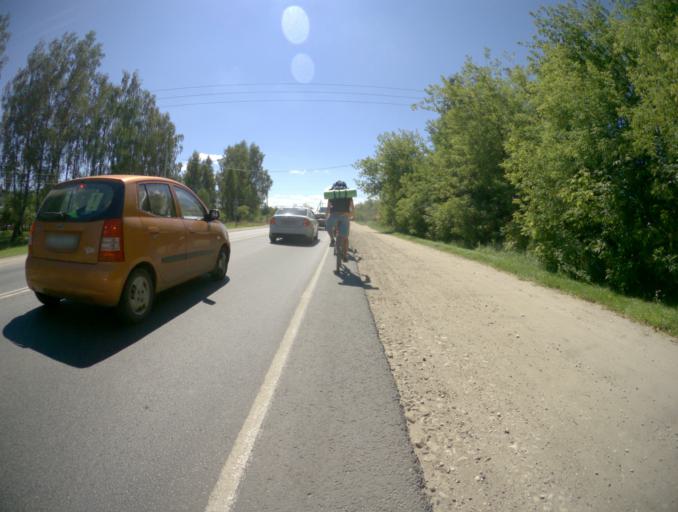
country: RU
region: Nizjnij Novgorod
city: Neklyudovo
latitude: 56.4106
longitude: 44.0101
